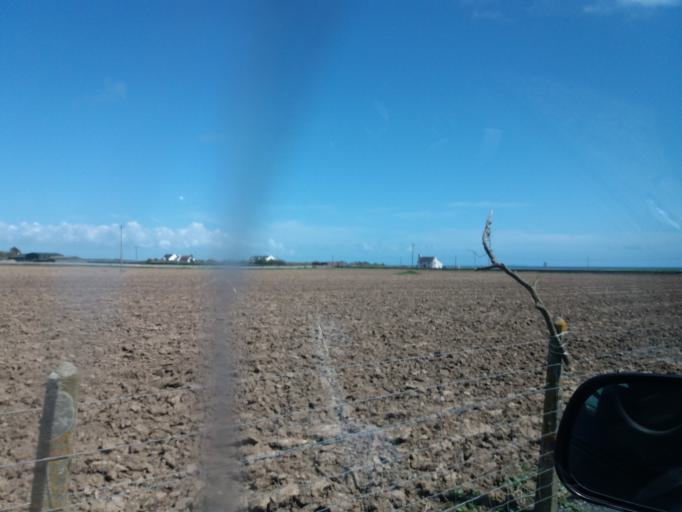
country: IE
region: Munster
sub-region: Waterford
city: Dunmore East
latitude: 52.1475
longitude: -6.9096
